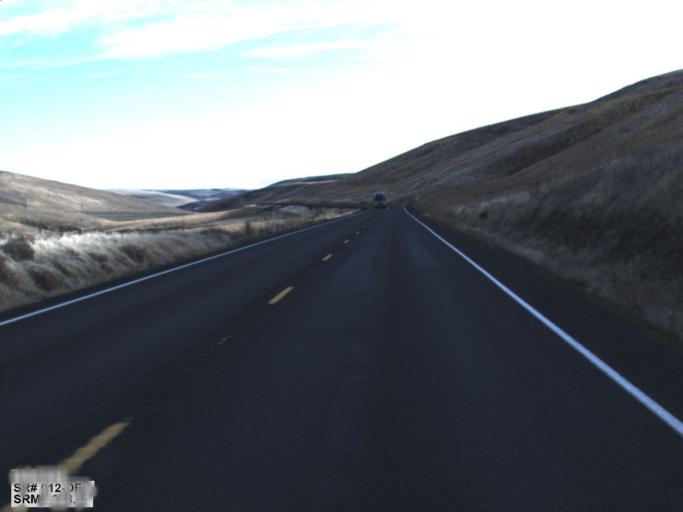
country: US
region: Washington
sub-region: Columbia County
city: Dayton
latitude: 46.4621
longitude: -117.9612
